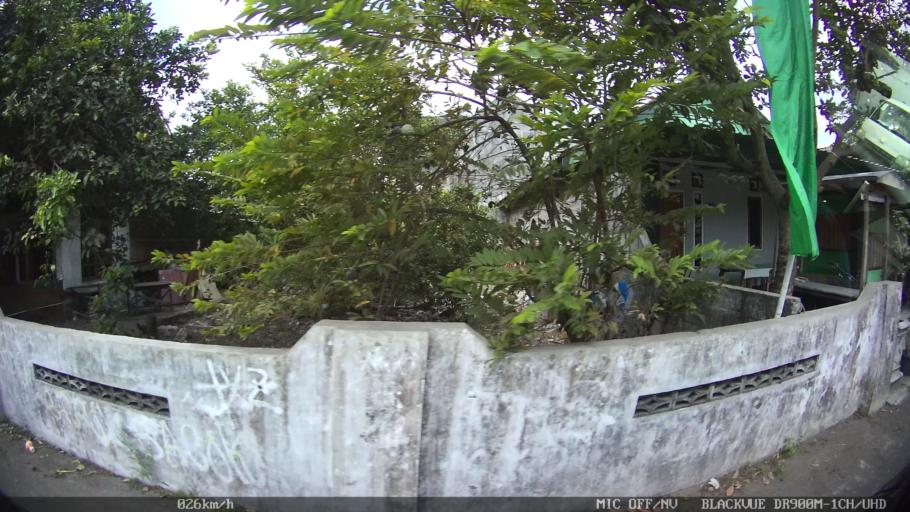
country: ID
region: Daerah Istimewa Yogyakarta
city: Gamping Lor
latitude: -7.8065
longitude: 110.3323
